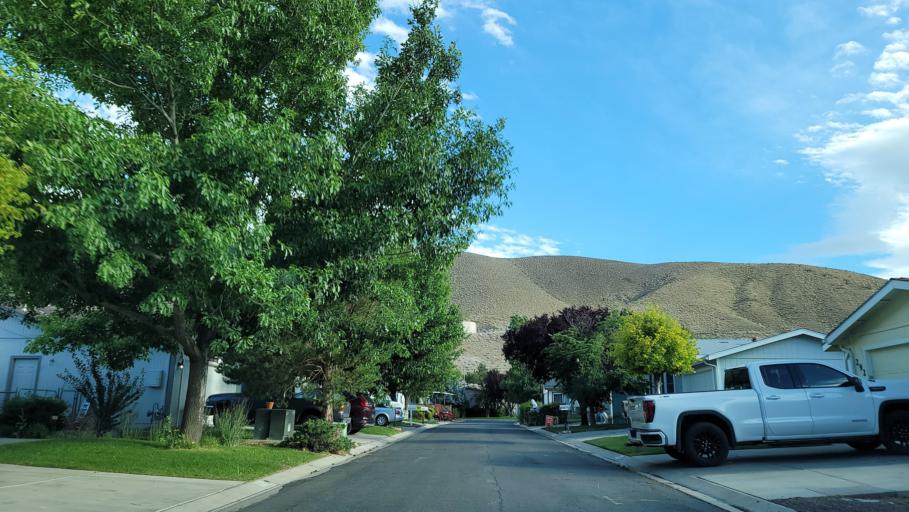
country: US
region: Nevada
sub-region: Washoe County
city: Sparks
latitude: 39.5113
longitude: -119.6395
